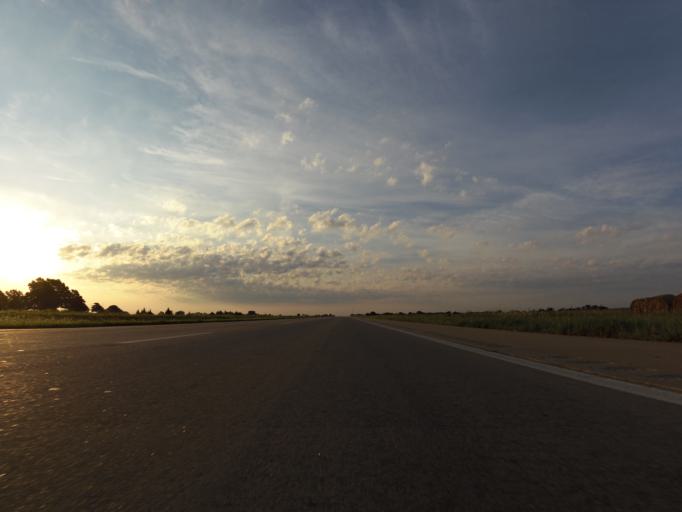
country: US
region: Kansas
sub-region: Reno County
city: Haven
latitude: 37.9263
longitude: -97.8428
